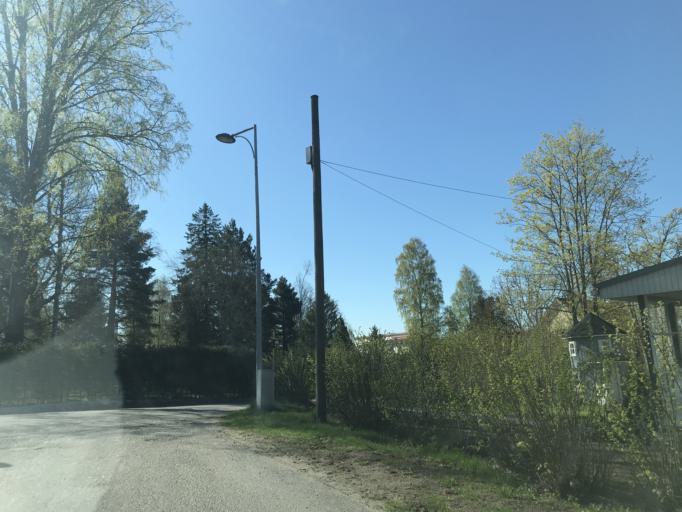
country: FI
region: Paijanne Tavastia
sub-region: Lahti
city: Orimattila
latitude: 60.8079
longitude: 25.7323
